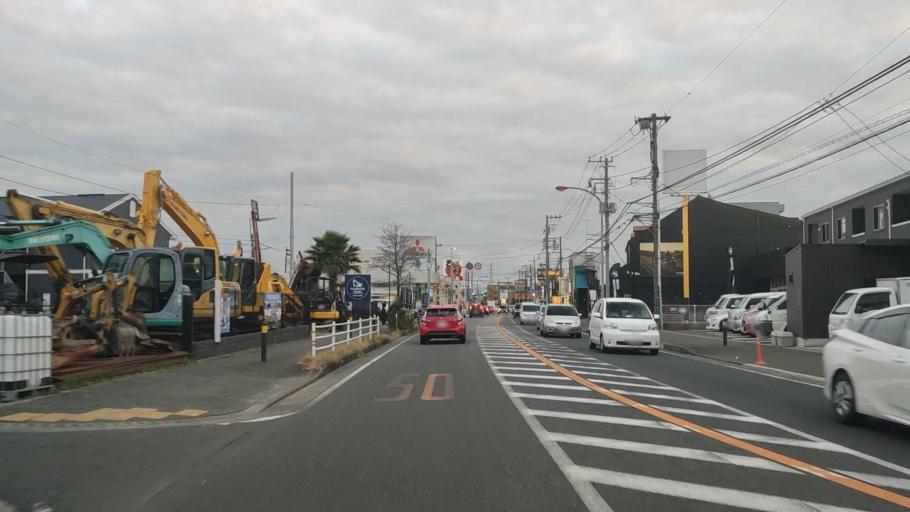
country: JP
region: Kanagawa
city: Minami-rinkan
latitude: 35.4222
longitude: 139.4690
